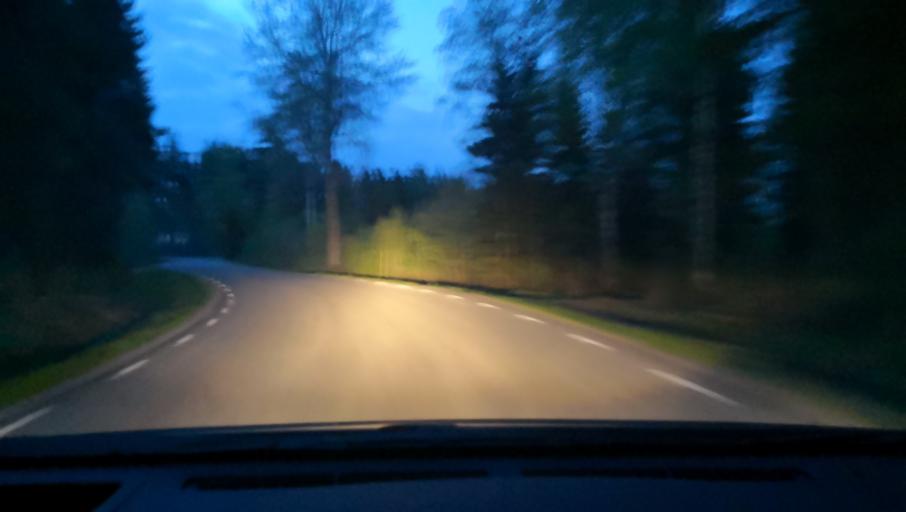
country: SE
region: OErebro
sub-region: Kumla Kommun
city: Kumla
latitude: 59.1917
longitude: 15.0566
